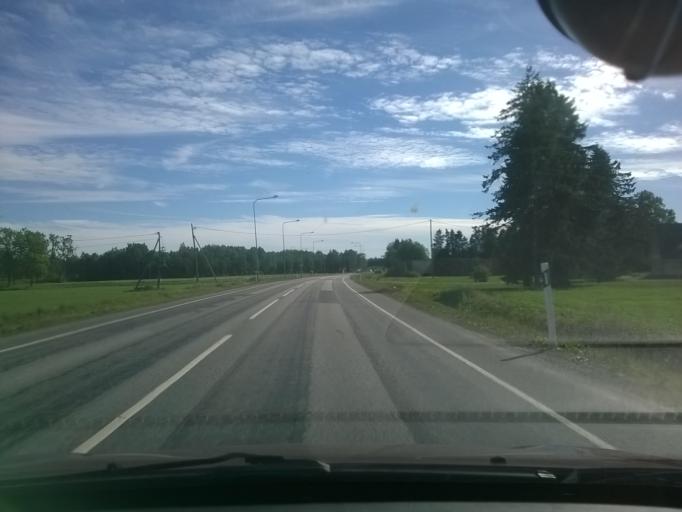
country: EE
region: Jaervamaa
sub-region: Paide linn
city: Paide
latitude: 58.9413
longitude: 25.6414
